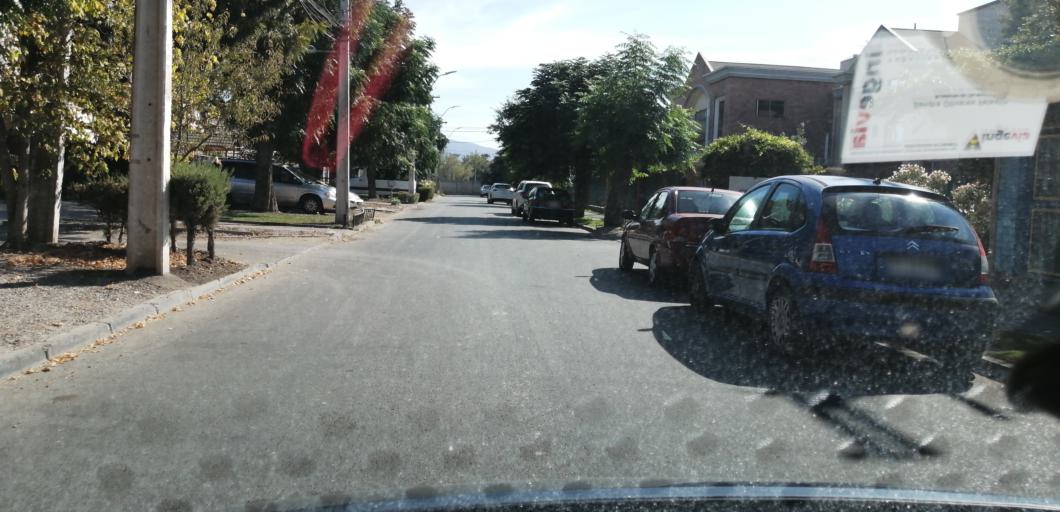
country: CL
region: Santiago Metropolitan
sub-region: Provincia de Santiago
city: Lo Prado
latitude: -33.4595
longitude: -70.7242
